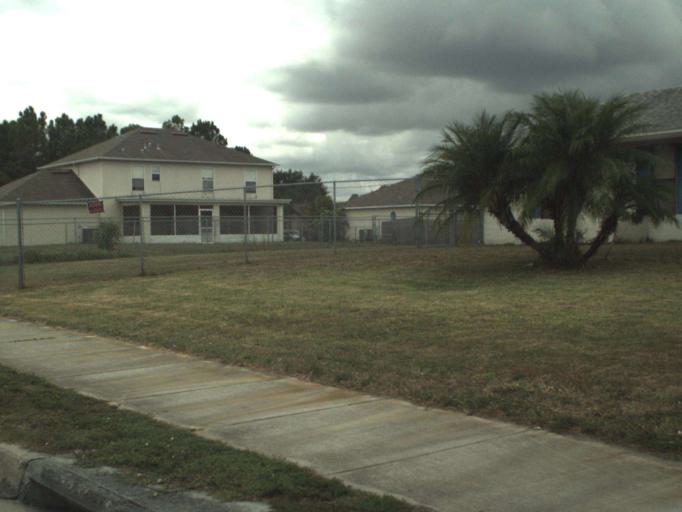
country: US
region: Florida
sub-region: Saint Lucie County
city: Port Saint Lucie
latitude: 27.2960
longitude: -80.3498
